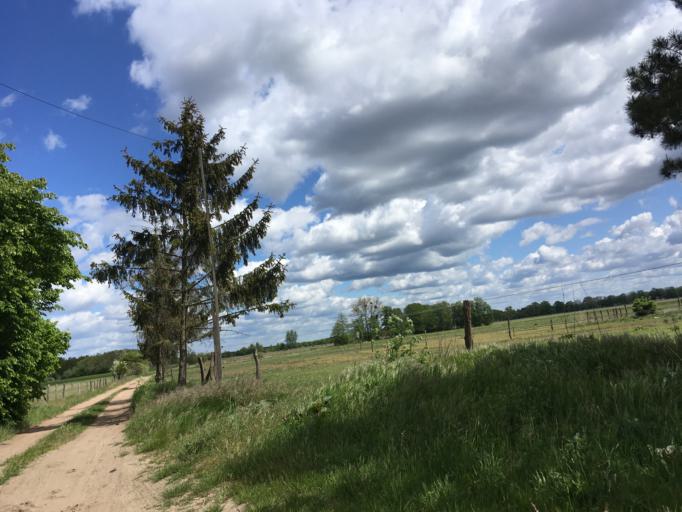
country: DE
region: Brandenburg
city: Liebenwalde
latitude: 52.8819
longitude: 13.4140
